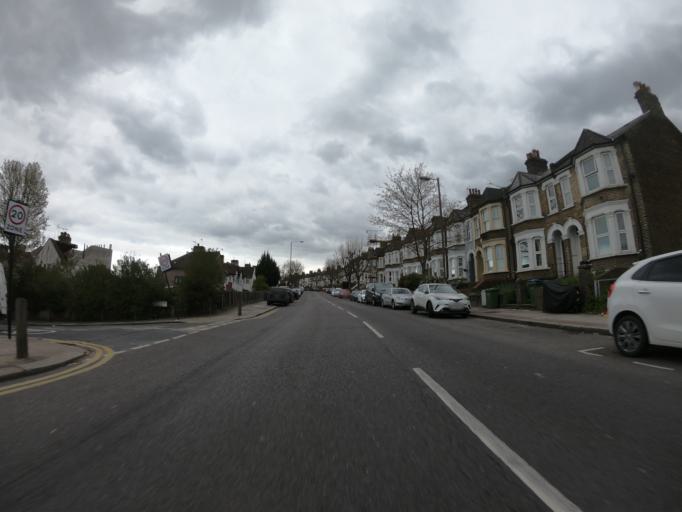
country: GB
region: England
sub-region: Greater London
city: Abbey Wood
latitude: 51.4815
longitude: 0.1018
